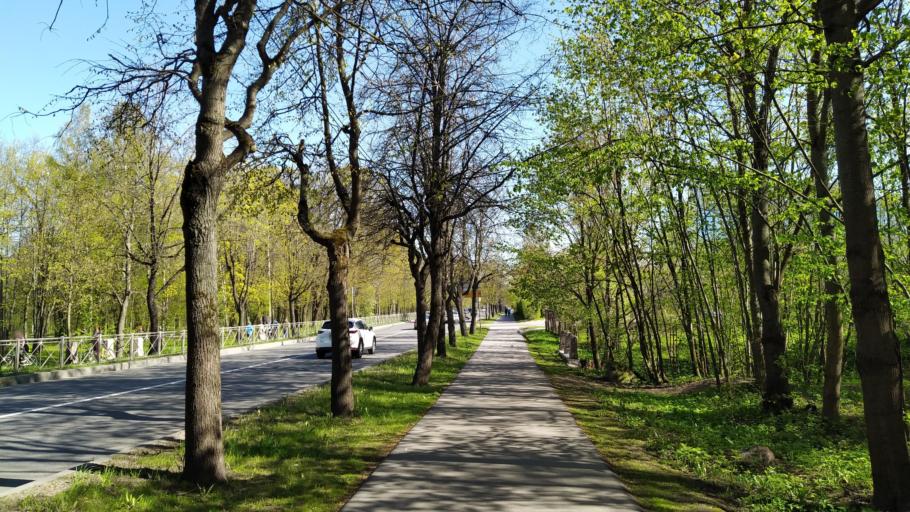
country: RU
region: St.-Petersburg
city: Pavlovsk
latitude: 59.7014
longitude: 30.4214
